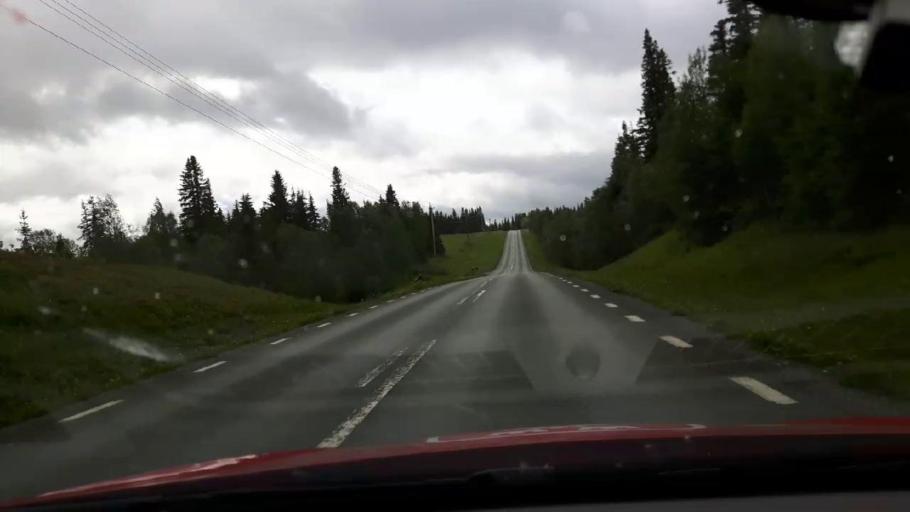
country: SE
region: Jaemtland
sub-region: Are Kommun
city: Are
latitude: 63.3764
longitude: 12.7227
